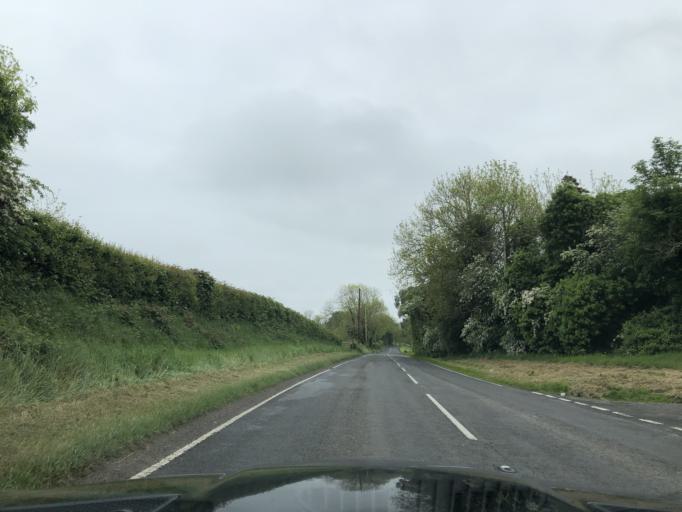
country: GB
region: Northern Ireland
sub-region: Down District
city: Killyleagh
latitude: 54.3645
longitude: -5.6090
